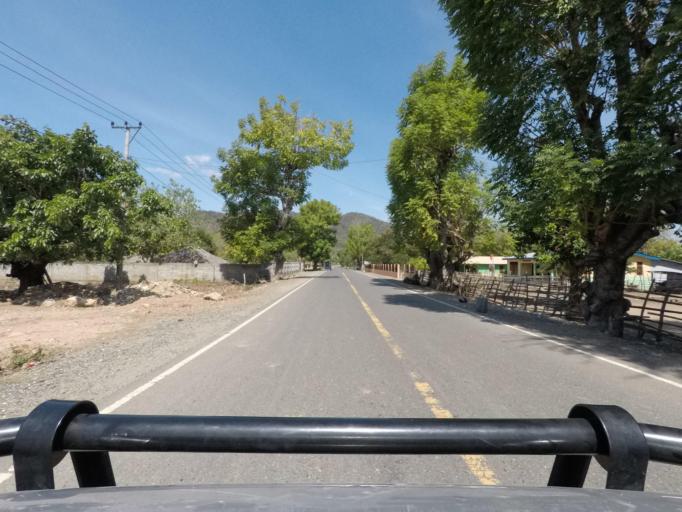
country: TL
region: Liquica
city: Maubara
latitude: -8.7913
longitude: 125.1015
